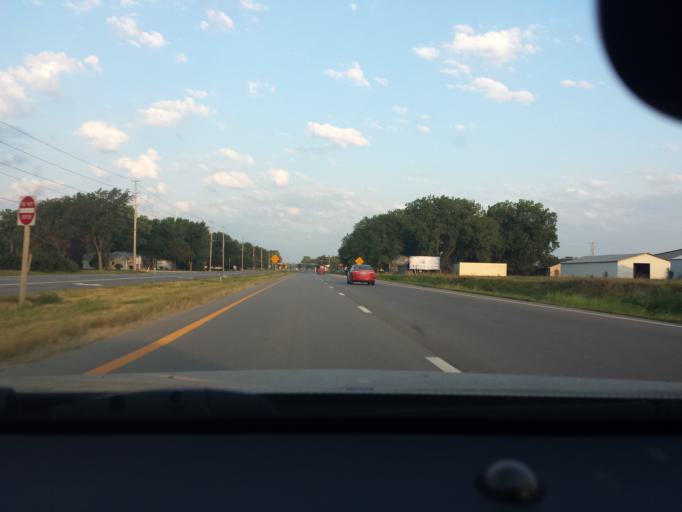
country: US
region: Kansas
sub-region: Riley County
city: Manhattan
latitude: 39.1963
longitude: -96.5044
